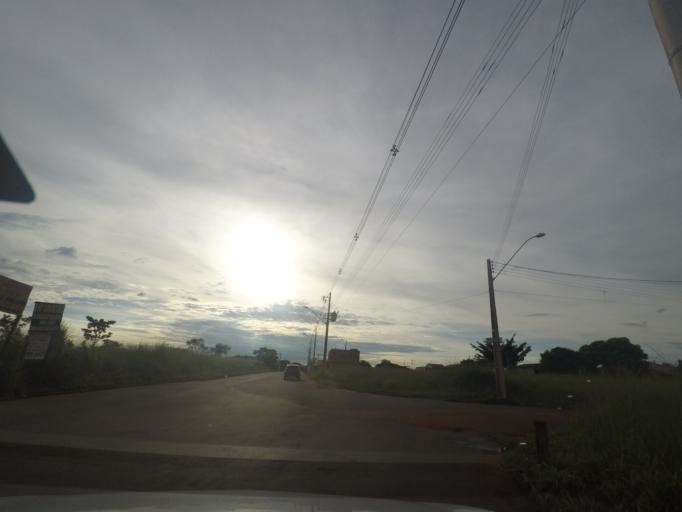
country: BR
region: Goias
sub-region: Trindade
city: Trindade
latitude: -16.7163
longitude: -49.3843
